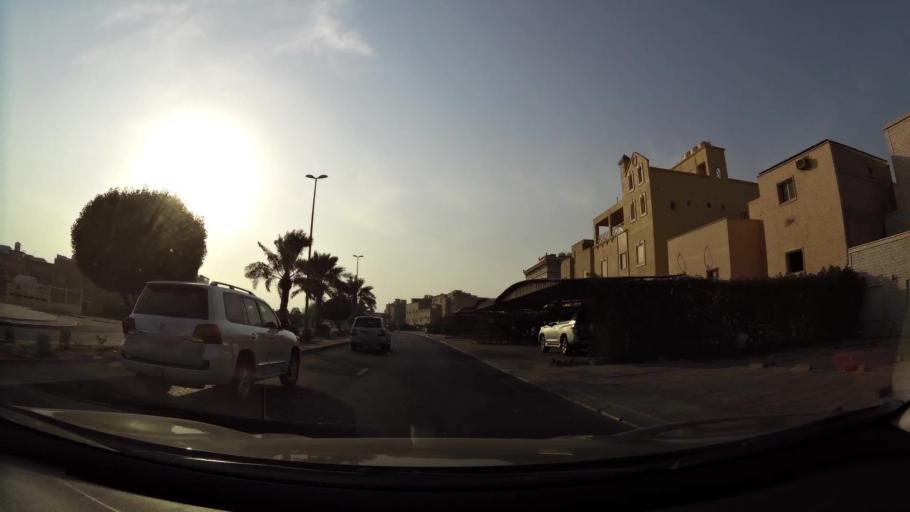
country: KW
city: Al Funaytis
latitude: 29.2220
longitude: 48.0665
